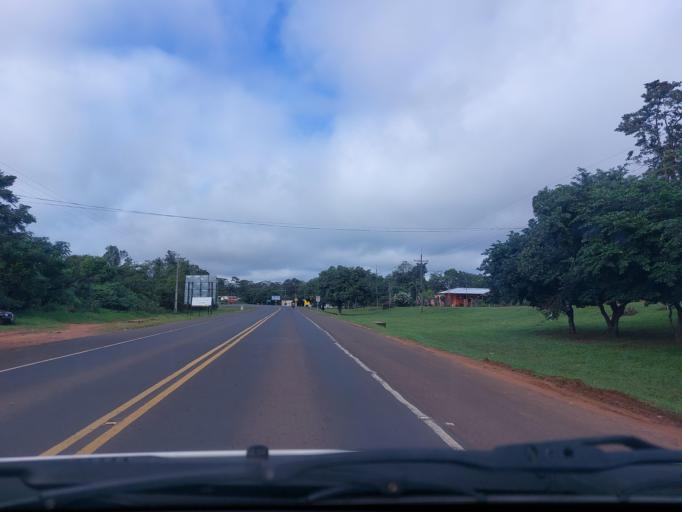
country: PY
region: San Pedro
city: Guayaybi
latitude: -24.5818
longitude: -56.4022
